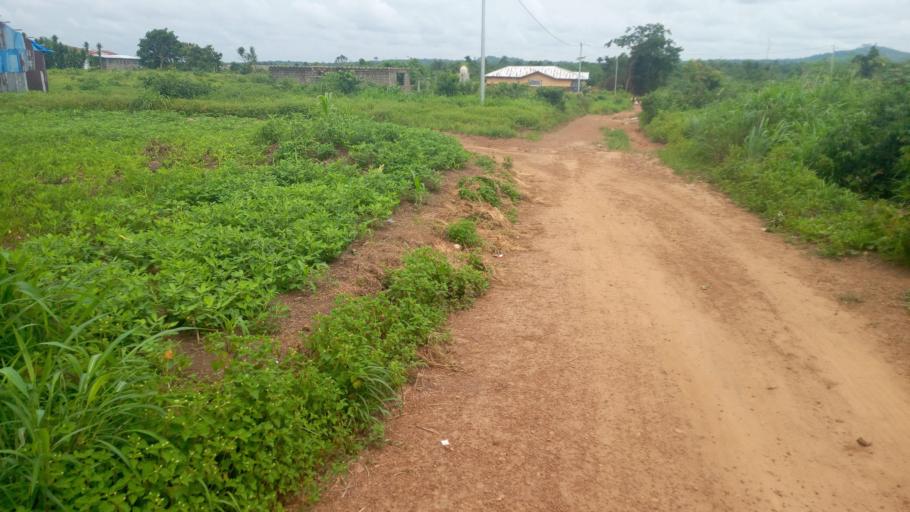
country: SL
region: Southern Province
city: Mogbwemo
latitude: 7.7764
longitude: -12.3026
